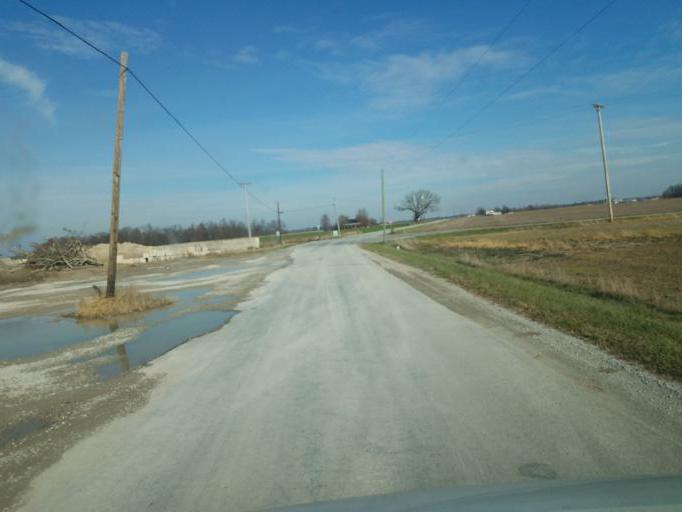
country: US
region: Ohio
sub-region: Hardin County
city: Forest
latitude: 40.6742
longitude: -83.4407
